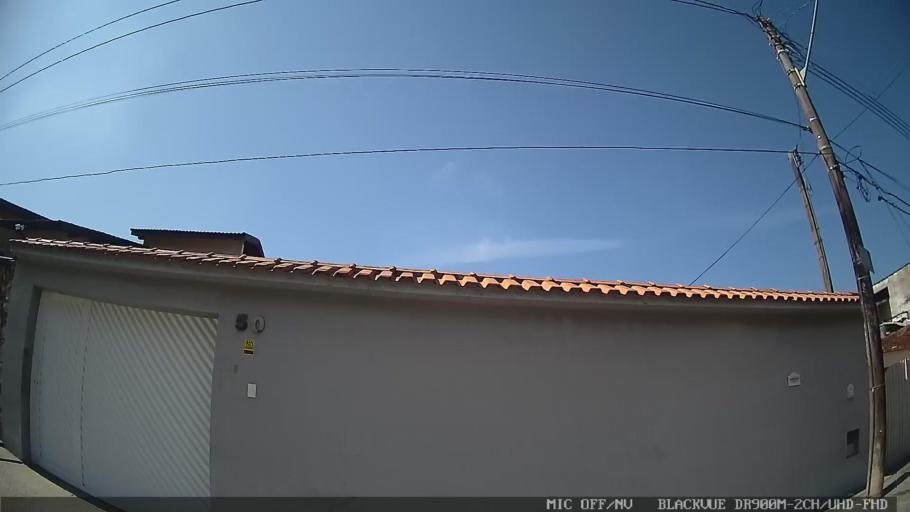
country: BR
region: Sao Paulo
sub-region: Guaruja
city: Guaruja
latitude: -24.0117
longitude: -46.2805
